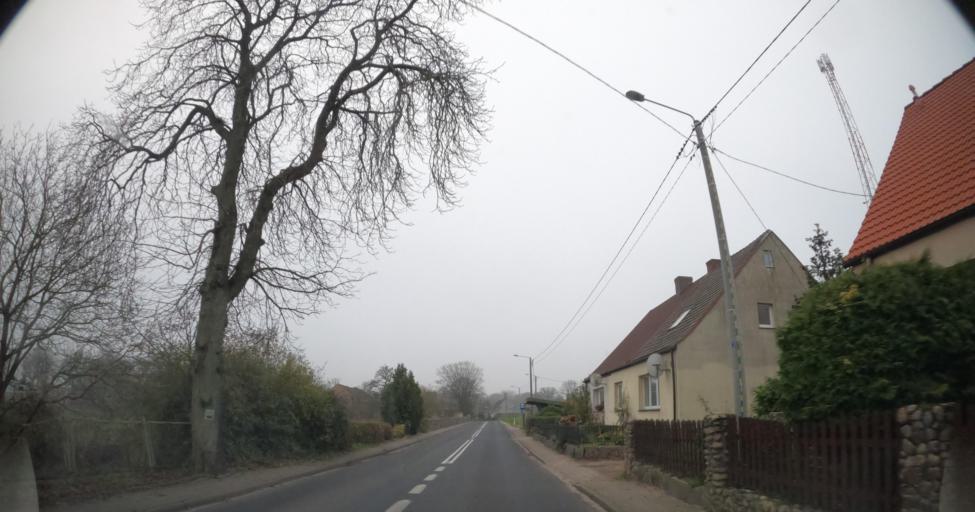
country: PL
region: West Pomeranian Voivodeship
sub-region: Powiat drawski
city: Drawsko Pomorskie
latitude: 53.5886
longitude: 15.7331
